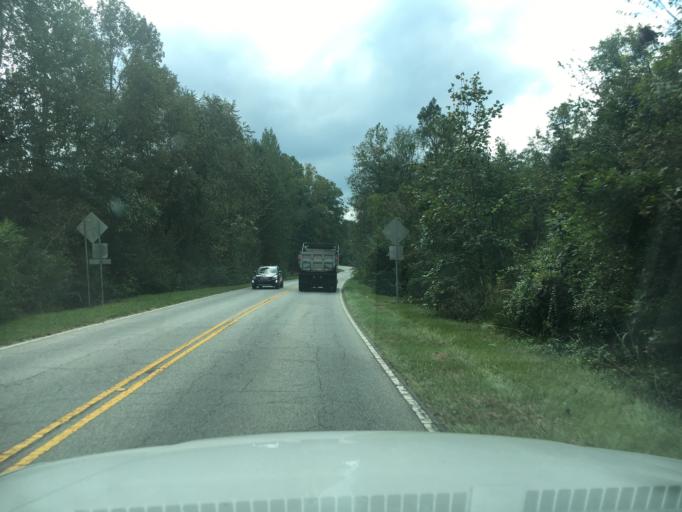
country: US
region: South Carolina
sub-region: Greenville County
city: Greer
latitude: 35.0234
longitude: -82.2665
